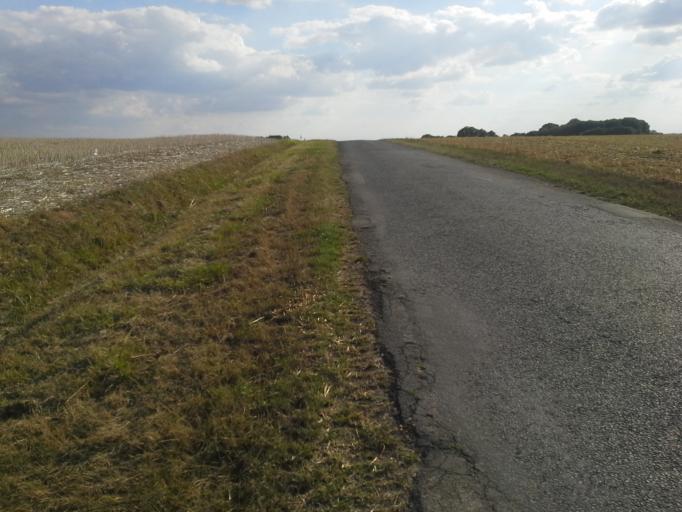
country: FR
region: Centre
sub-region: Departement du Loir-et-Cher
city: Villiers-sur-Loir
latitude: 47.8189
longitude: 0.9936
